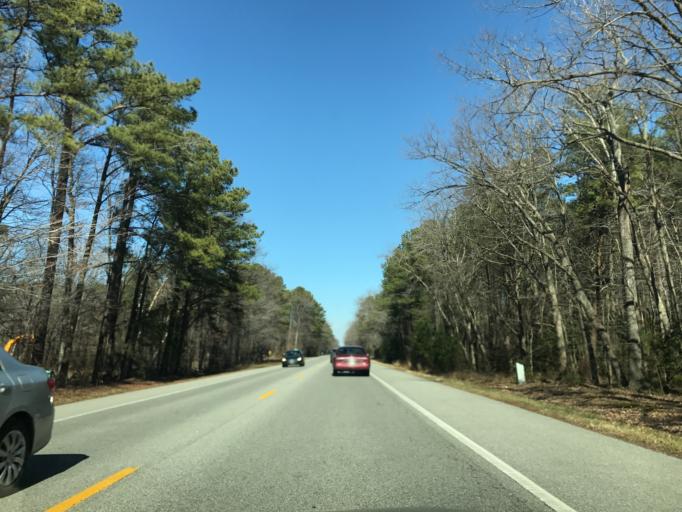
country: US
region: Maryland
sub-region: Queen Anne's County
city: Stevensville
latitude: 38.9441
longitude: -76.3532
